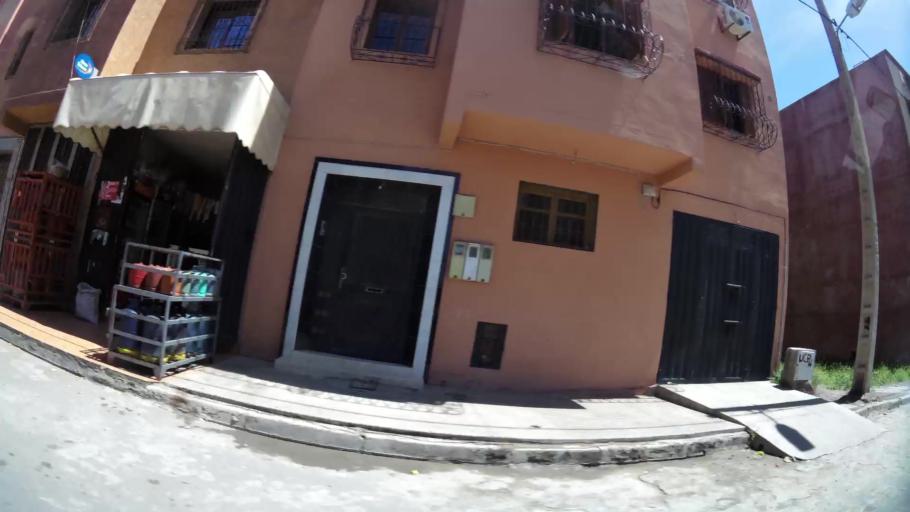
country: MA
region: Marrakech-Tensift-Al Haouz
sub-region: Marrakech
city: Marrakesh
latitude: 31.6380
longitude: -8.0489
